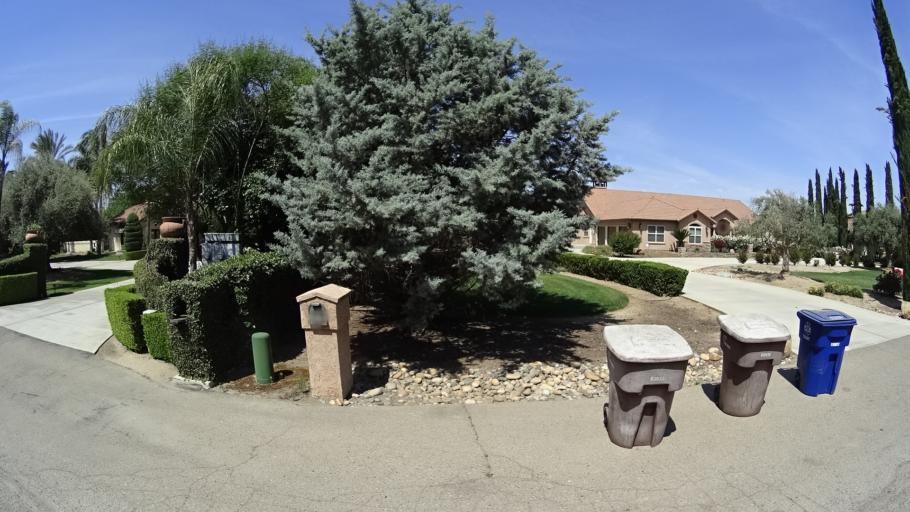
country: US
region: California
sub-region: Kings County
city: Armona
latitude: 36.3404
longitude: -119.7045
